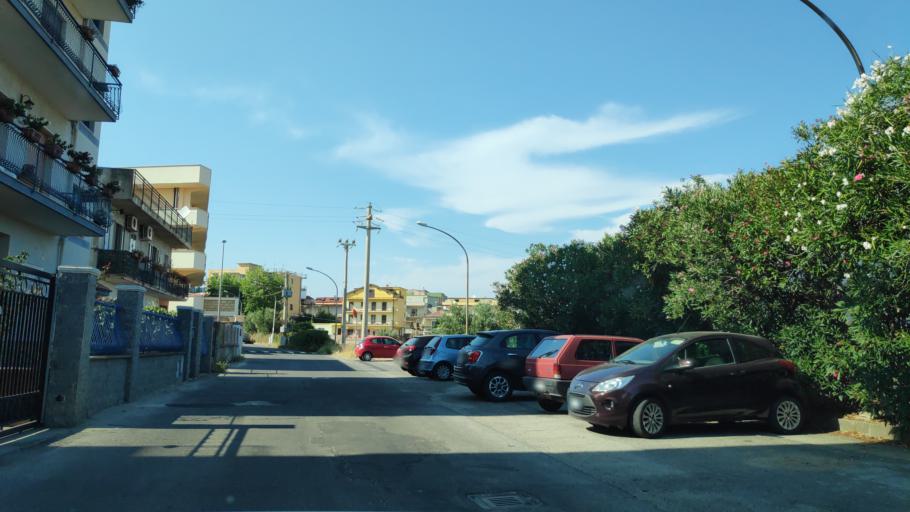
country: IT
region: Calabria
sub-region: Provincia di Catanzaro
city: Soverato Superiore
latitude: 38.6881
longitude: 16.5348
